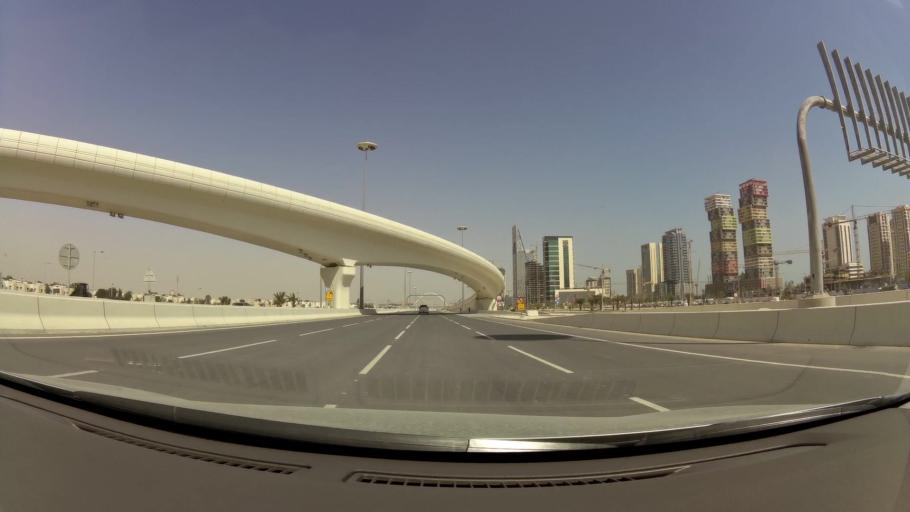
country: QA
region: Baladiyat ad Dawhah
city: Doha
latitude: 25.3819
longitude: 51.5213
